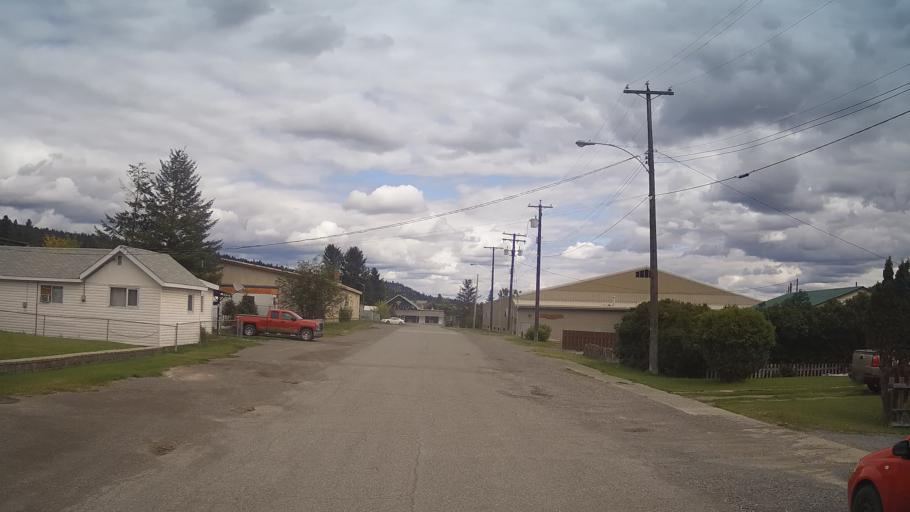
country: CA
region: British Columbia
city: Cache Creek
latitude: 51.0904
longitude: -121.5866
